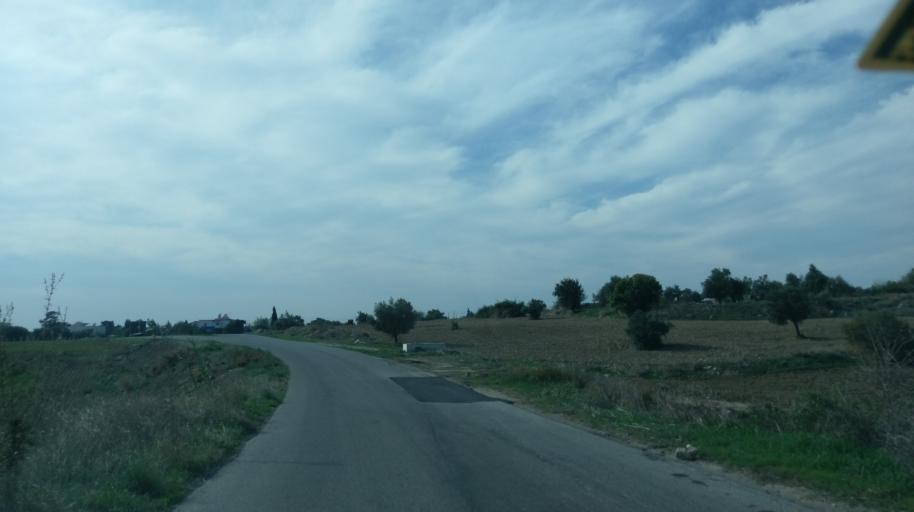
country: CY
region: Keryneia
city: Lapithos
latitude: 35.2787
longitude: 33.1775
